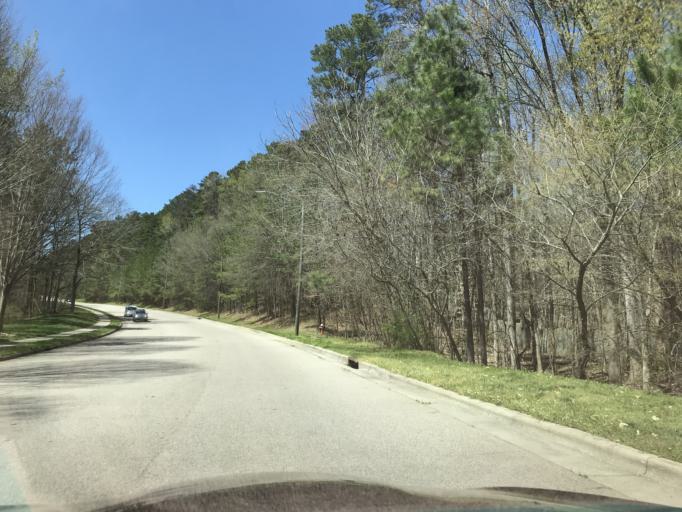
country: US
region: North Carolina
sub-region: Wake County
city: Cary
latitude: 35.8768
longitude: -78.7225
